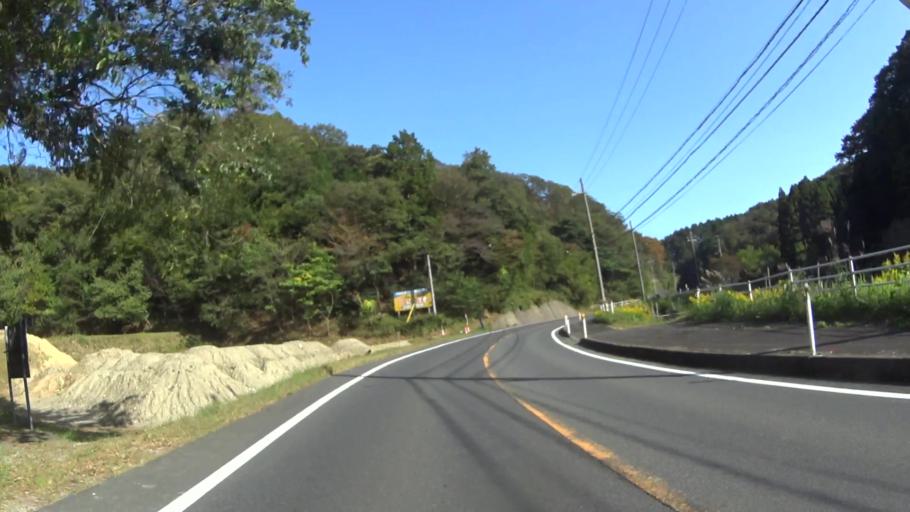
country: JP
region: Hyogo
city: Toyooka
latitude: 35.6598
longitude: 134.9979
